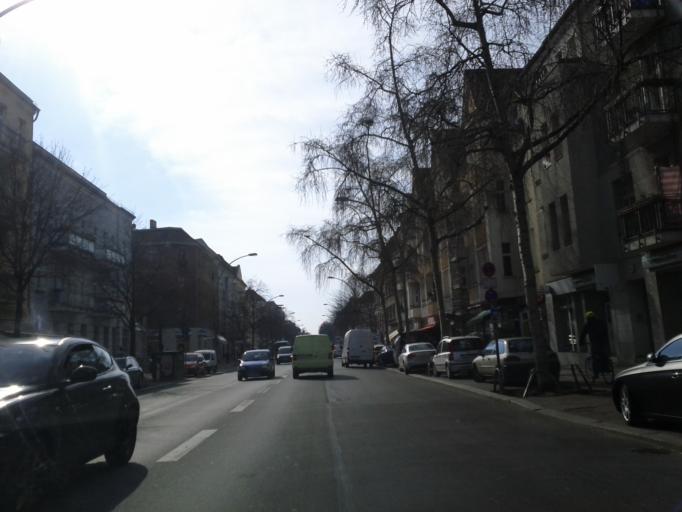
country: DE
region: Berlin
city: Baumschulenweg
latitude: 52.4668
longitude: 13.4885
